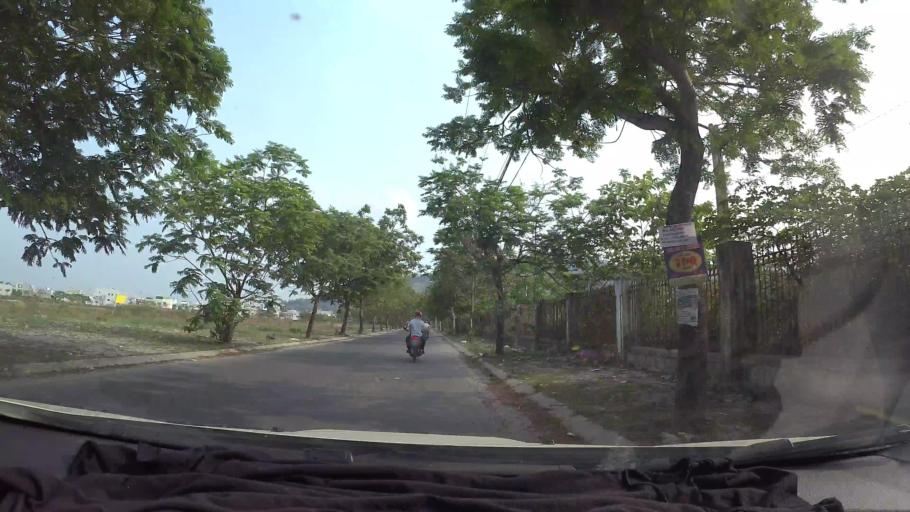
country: VN
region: Da Nang
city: Lien Chieu
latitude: 16.0490
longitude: 108.1627
